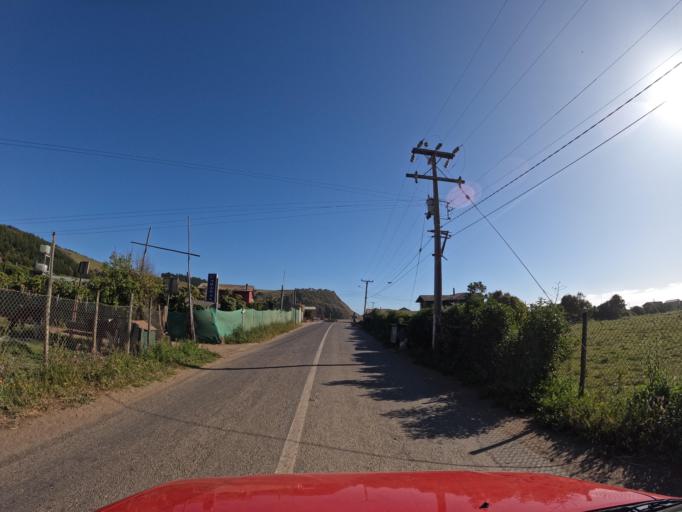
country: CL
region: Maule
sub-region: Provincia de Talca
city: Constitucion
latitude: -34.8532
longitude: -72.1421
